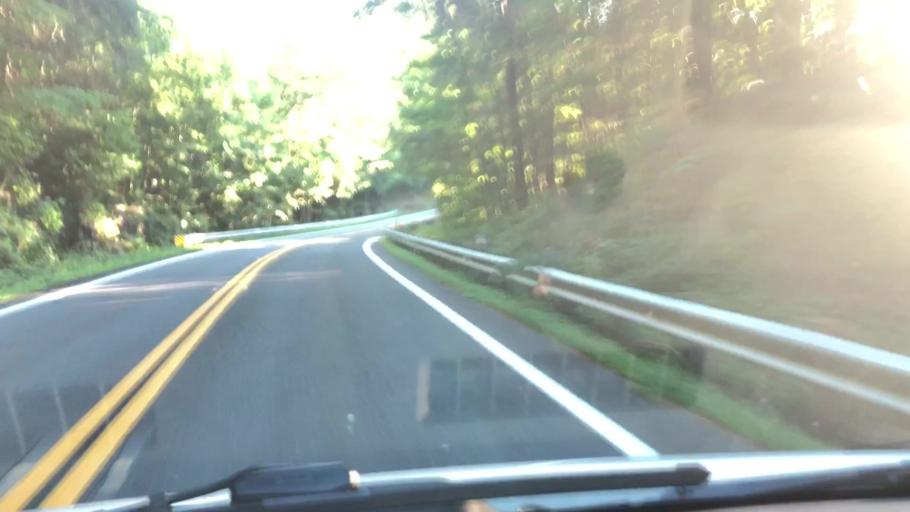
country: US
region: Massachusetts
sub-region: Hampshire County
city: Westhampton
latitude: 42.2984
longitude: -72.8682
